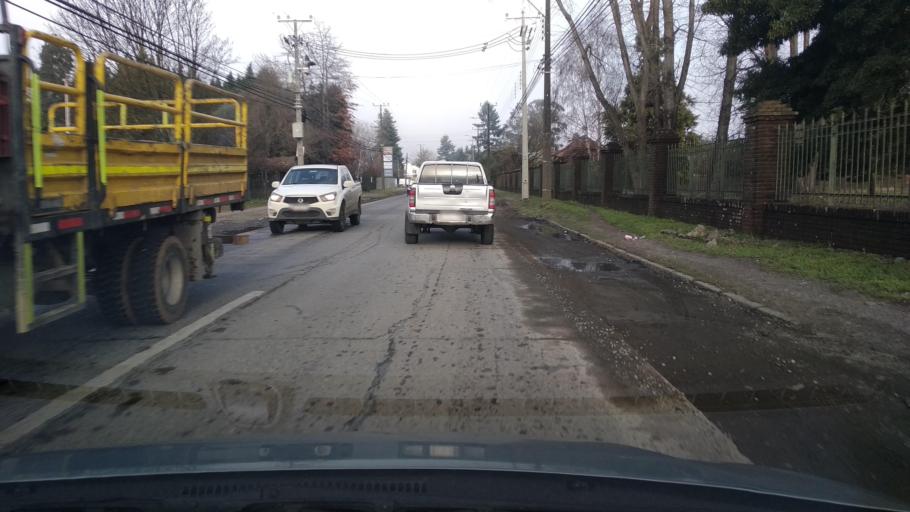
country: CL
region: Los Rios
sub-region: Provincia de Valdivia
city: Valdivia
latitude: -39.8102
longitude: -73.2330
